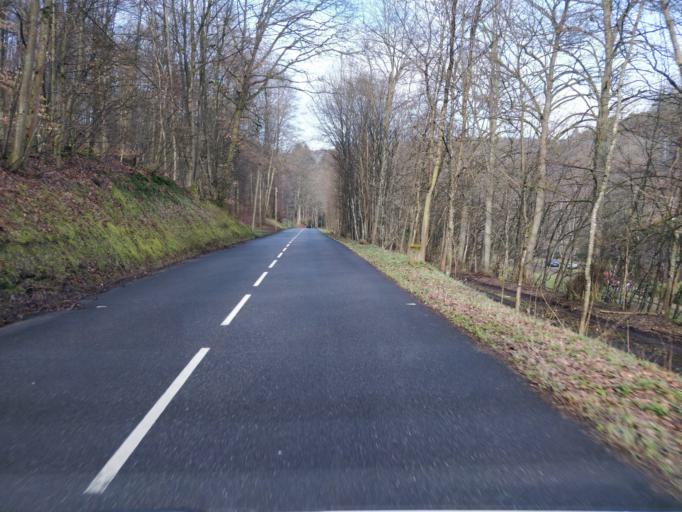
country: FR
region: Lorraine
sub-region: Departement de la Moselle
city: Soucht
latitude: 48.9218
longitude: 7.3015
